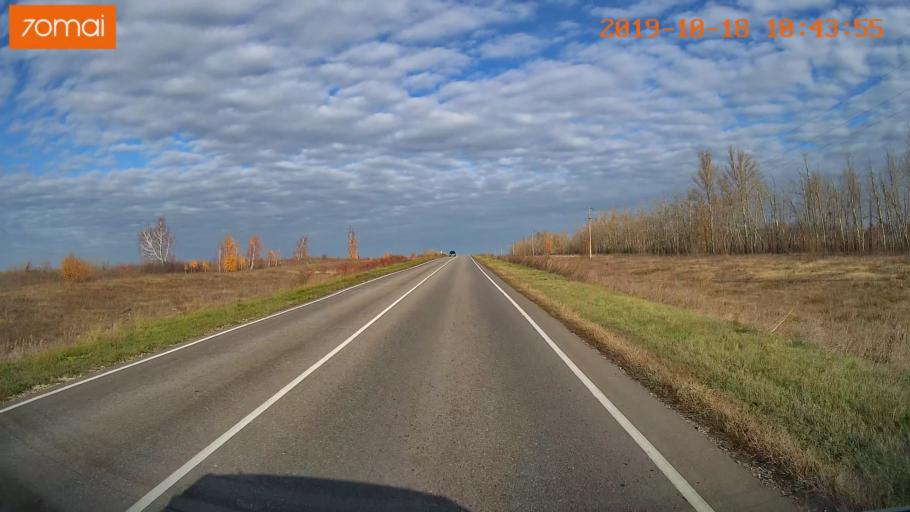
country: RU
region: Tula
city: Yepifan'
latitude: 53.6471
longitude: 38.6832
